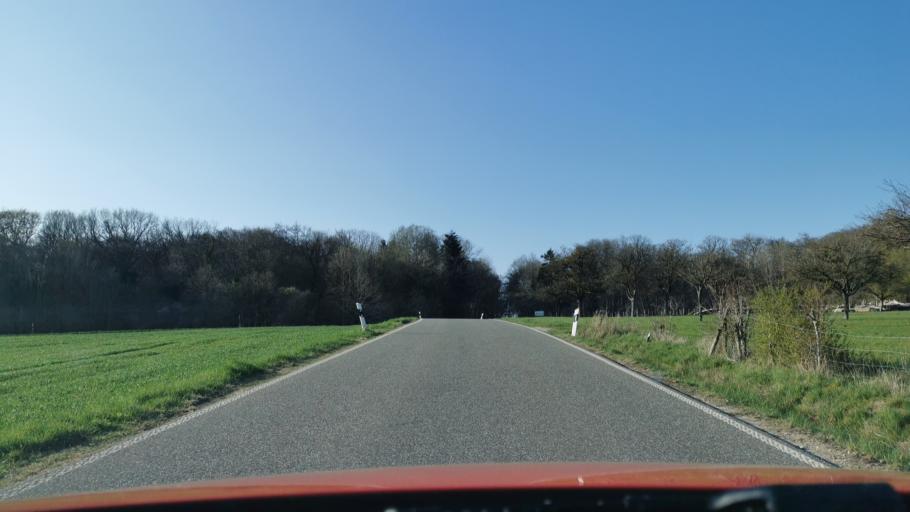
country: DE
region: Rheinland-Pfalz
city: Trierweiler
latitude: 49.7646
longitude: 6.5545
